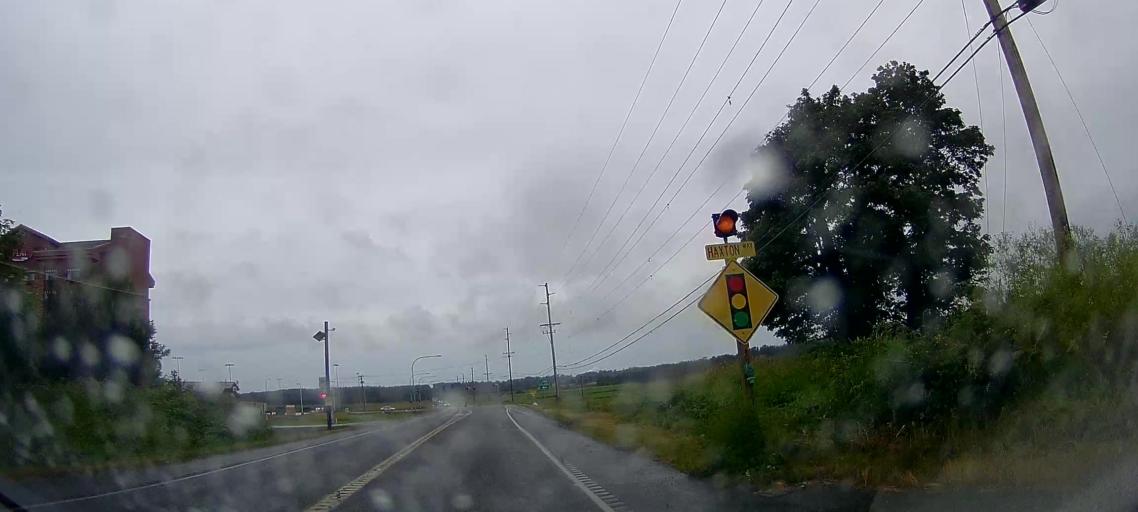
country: US
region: Washington
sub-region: Whatcom County
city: Ferndale
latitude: 48.8196
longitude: -122.6262
